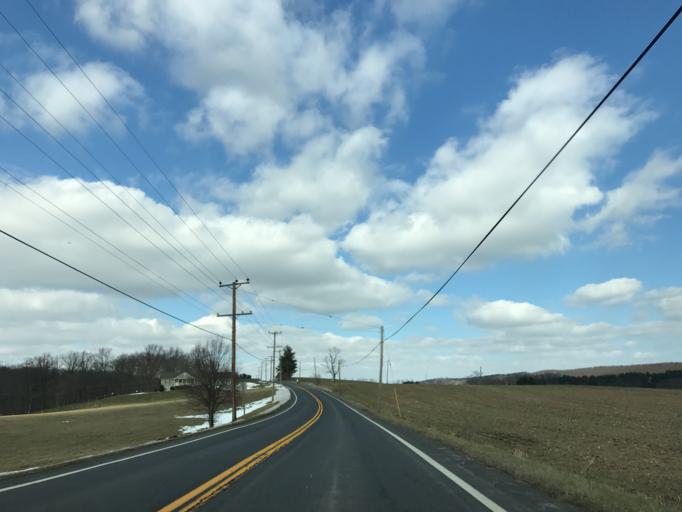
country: US
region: Maryland
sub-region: Carroll County
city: Manchester
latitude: 39.6689
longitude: -76.9375
